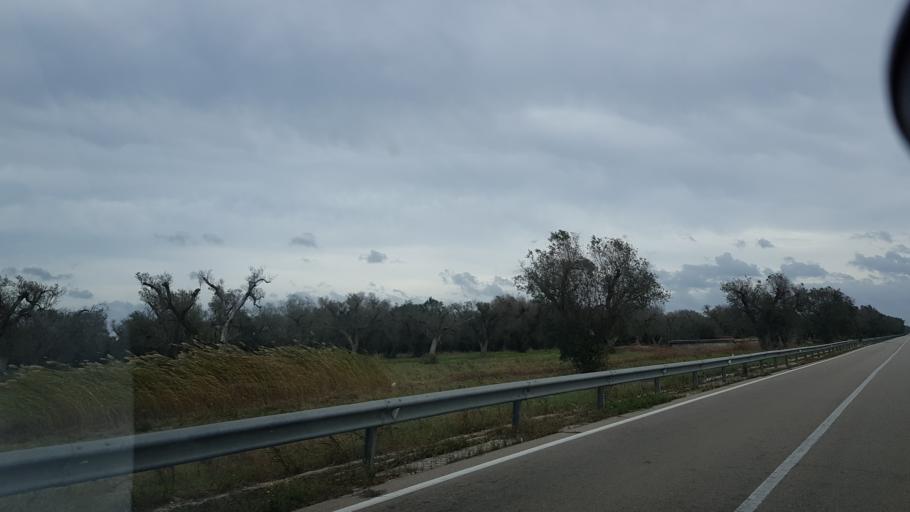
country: IT
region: Apulia
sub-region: Provincia di Brindisi
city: San Pancrazio Salentino
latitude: 40.4073
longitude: 17.8847
